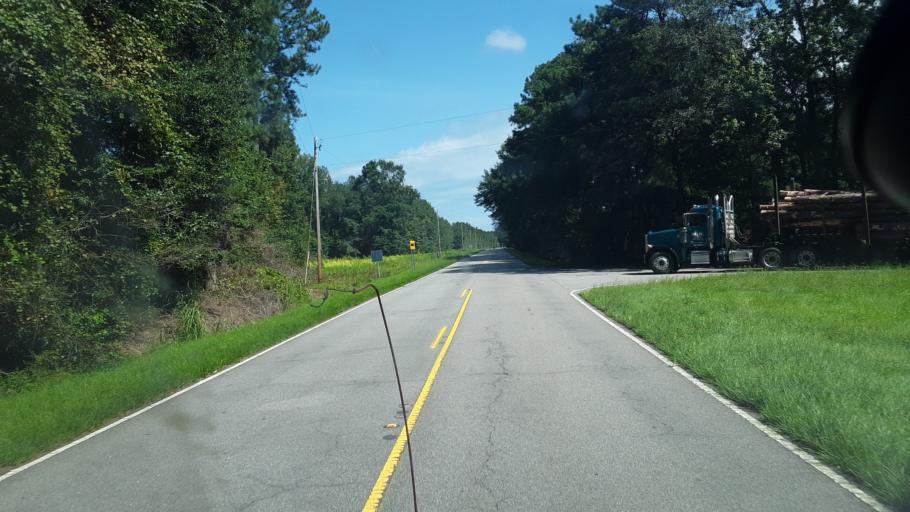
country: US
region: South Carolina
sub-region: Hampton County
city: Hampton
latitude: 33.0218
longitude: -81.0423
